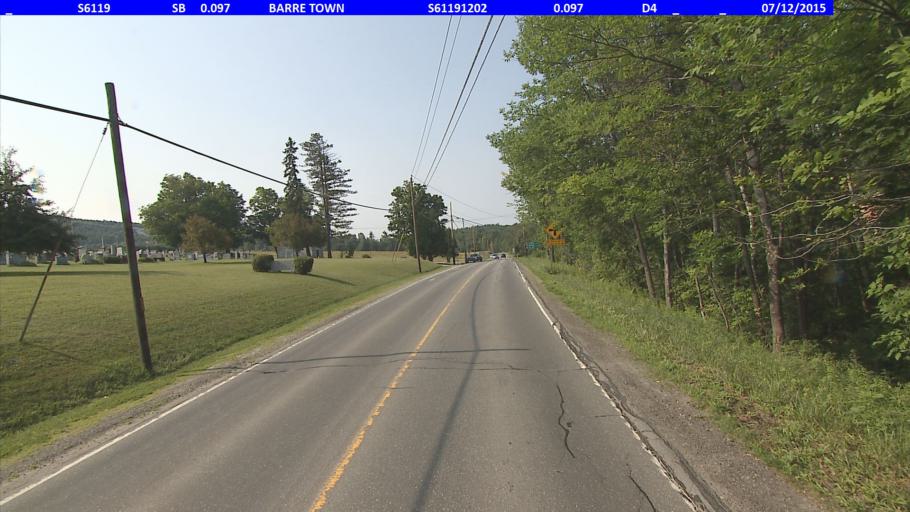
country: US
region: Vermont
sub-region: Washington County
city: South Barre
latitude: 44.1716
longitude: -72.4913
